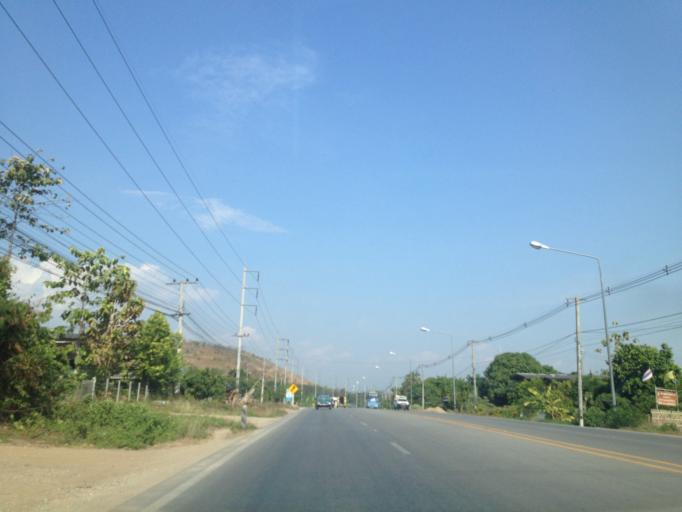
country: TH
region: Chiang Mai
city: Chom Thong
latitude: 18.3564
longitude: 98.6792
